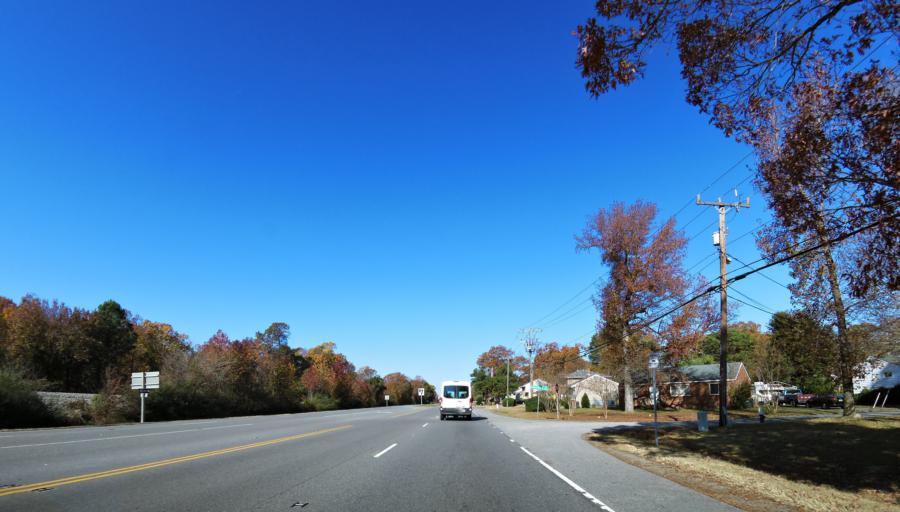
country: US
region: Virginia
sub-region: City of Williamsburg
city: Williamsburg
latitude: 37.2481
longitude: -76.6570
